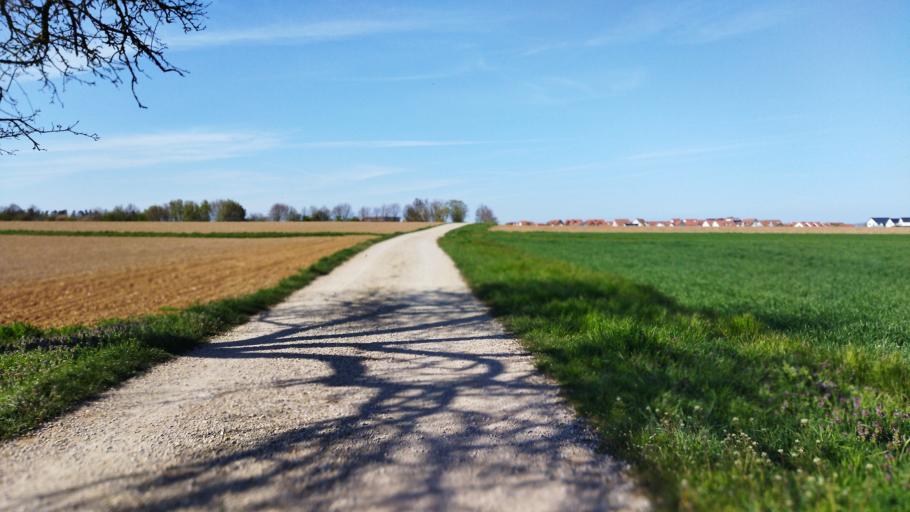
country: DE
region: Baden-Wuerttemberg
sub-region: Regierungsbezirk Stuttgart
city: Bad Wimpfen
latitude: 49.2174
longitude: 9.1478
